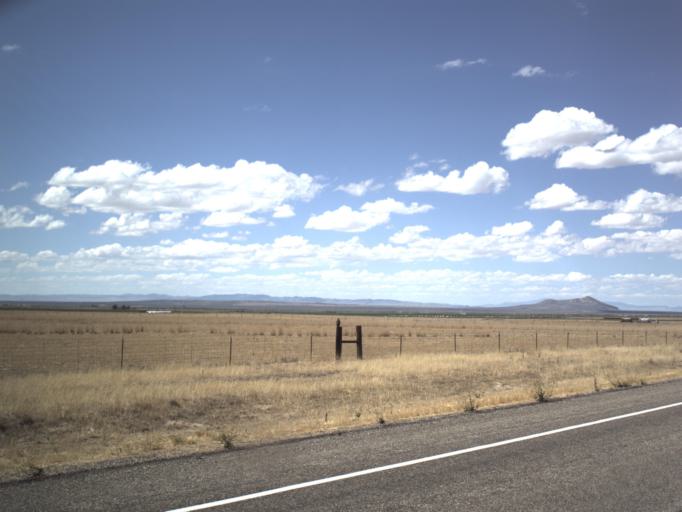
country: US
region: Utah
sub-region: Millard County
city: Fillmore
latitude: 39.1158
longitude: -112.3102
